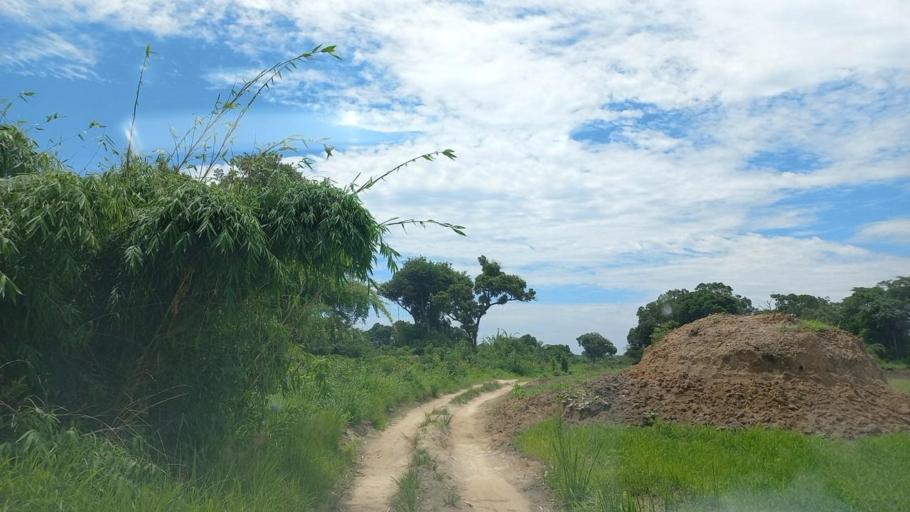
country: ZM
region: Copperbelt
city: Kitwe
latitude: -12.7996
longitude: 28.4014
